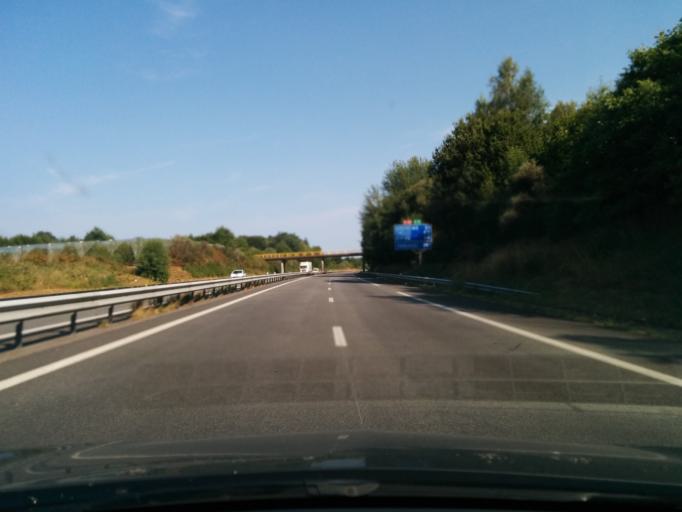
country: FR
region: Limousin
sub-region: Departement de la Haute-Vienne
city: Vicq-sur-Breuilh
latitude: 45.6431
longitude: 1.4148
